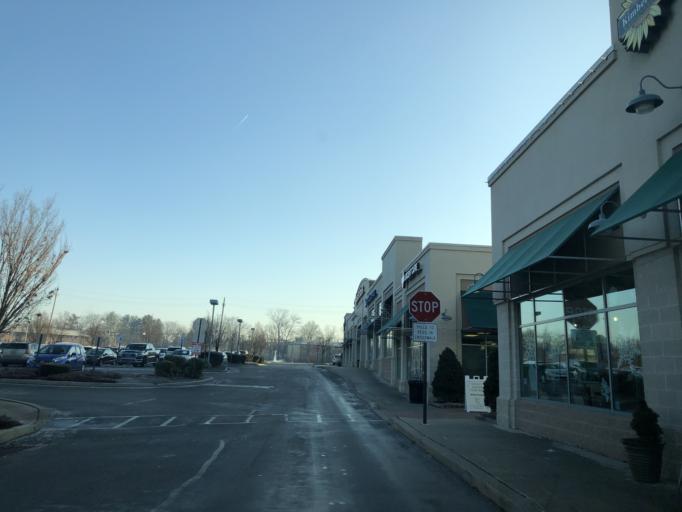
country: US
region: Pennsylvania
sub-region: Chester County
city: Downingtown
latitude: 40.0086
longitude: -75.7020
